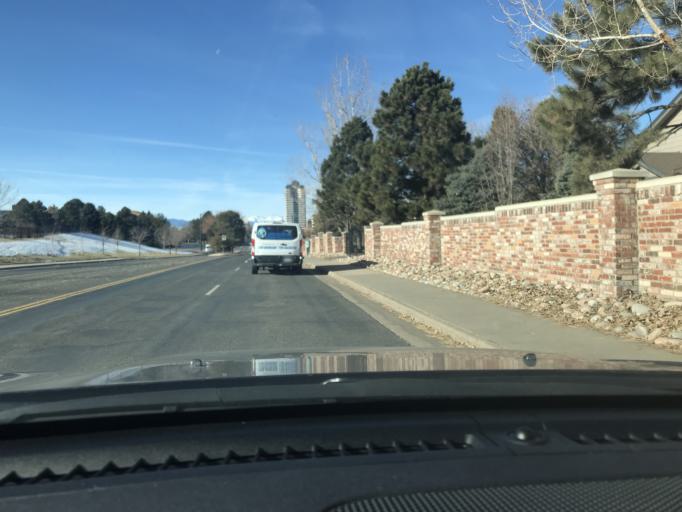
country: US
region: Colorado
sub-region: Arapahoe County
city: Centennial
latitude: 39.5987
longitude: -104.8785
